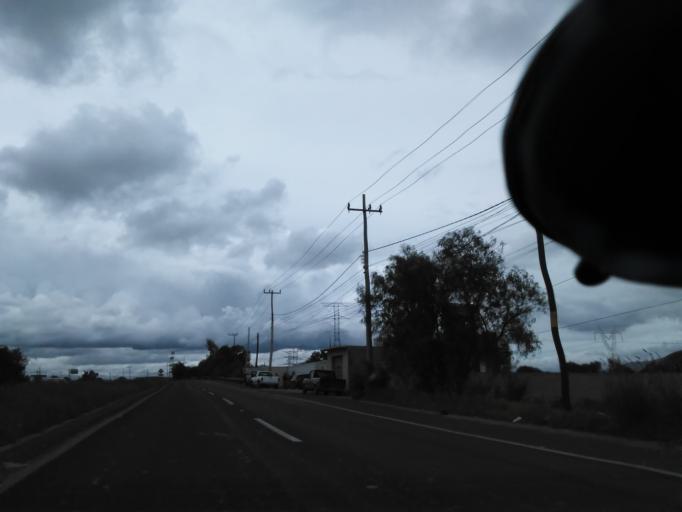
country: MX
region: Hidalgo
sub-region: Tula de Allende
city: Residencial Arboledas
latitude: 20.0617
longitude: -99.2730
